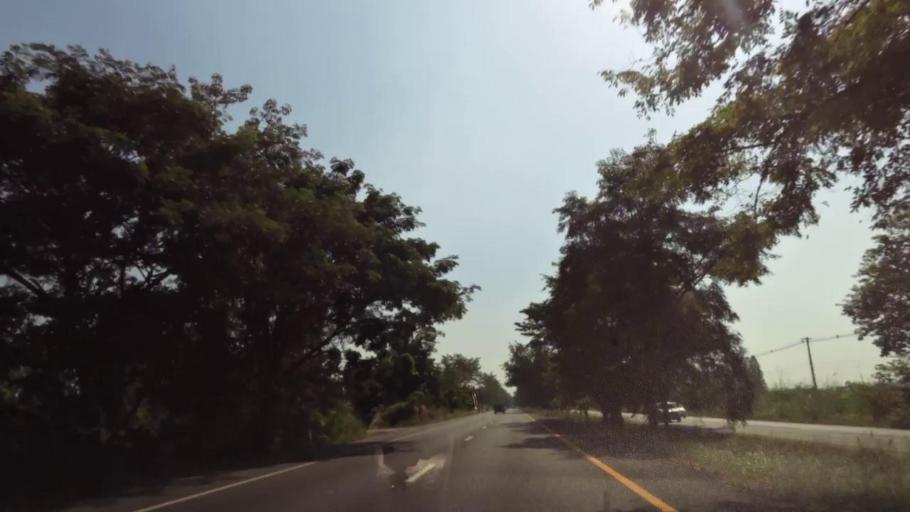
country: TH
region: Nakhon Sawan
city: Kao Liao
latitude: 15.9714
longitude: 100.1193
